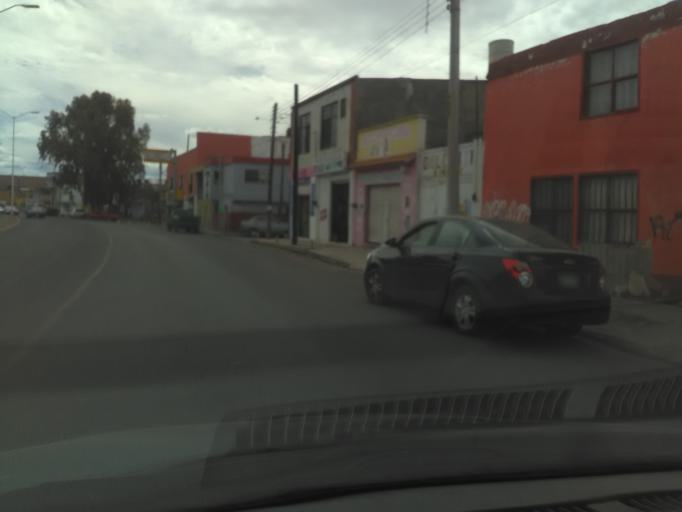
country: MX
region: Durango
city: Victoria de Durango
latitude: 24.0396
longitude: -104.6801
